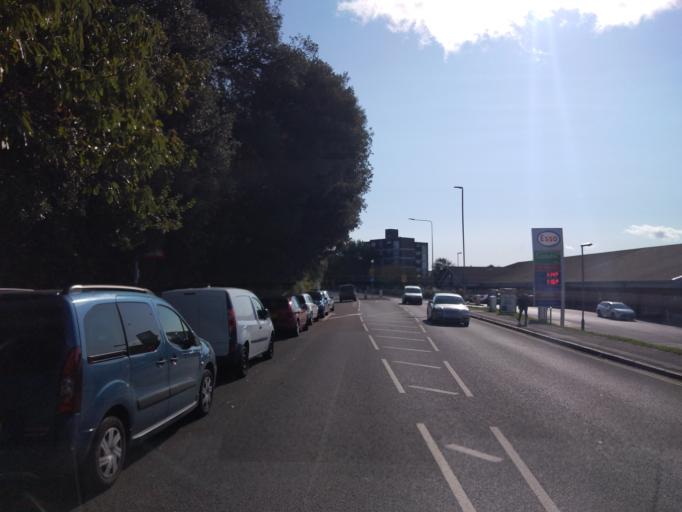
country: GB
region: England
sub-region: East Sussex
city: Hastings
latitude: 50.8606
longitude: 0.5622
